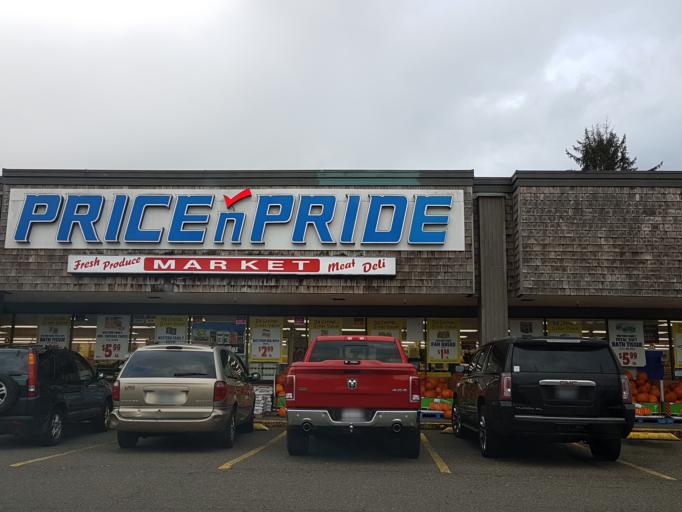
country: US
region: Oregon
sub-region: Douglas County
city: Reedsport
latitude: 43.6996
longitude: -124.1089
